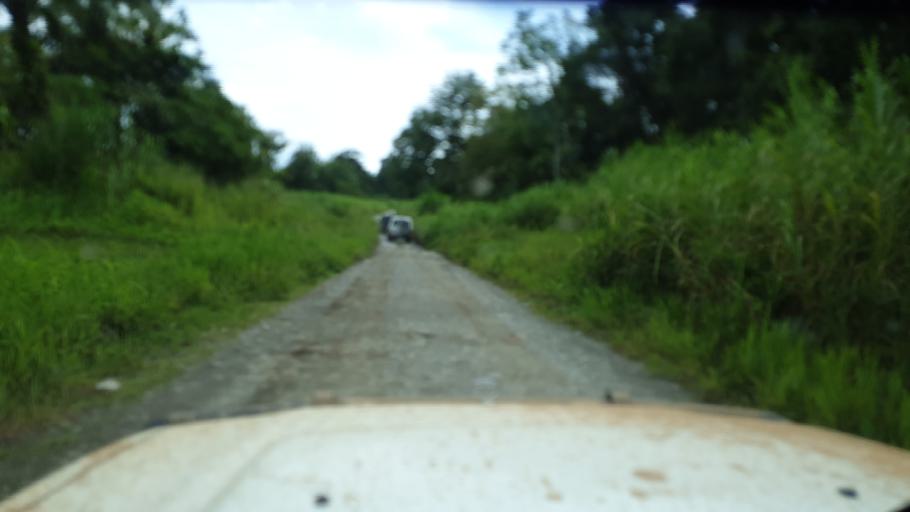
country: PG
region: Northern Province
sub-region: Sohe
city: Kokoda
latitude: -8.9163
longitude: 147.8556
